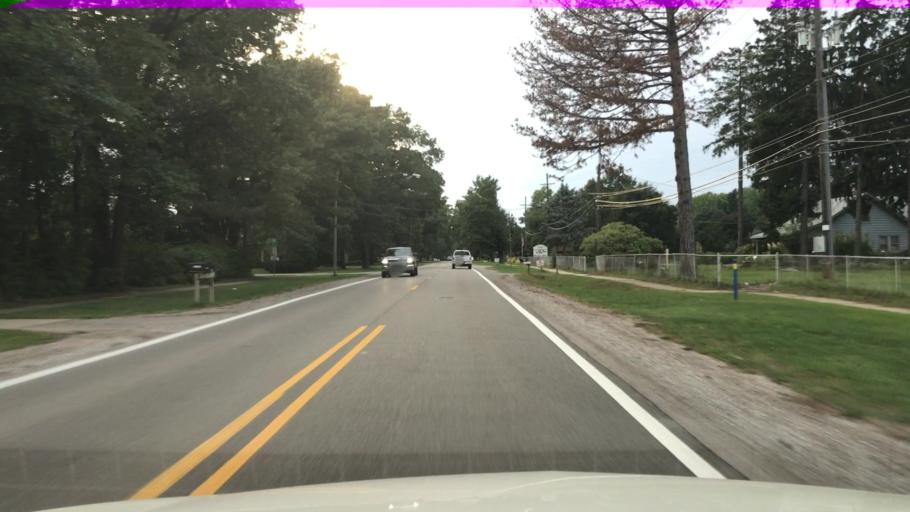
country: US
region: Michigan
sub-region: Macomb County
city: Shelby
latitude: 42.6831
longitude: -83.0696
